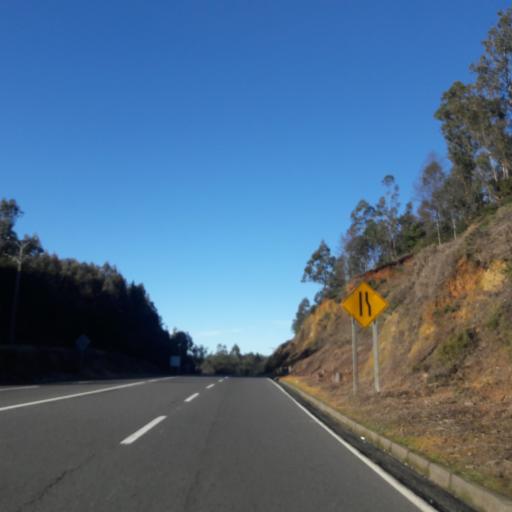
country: CL
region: Biobio
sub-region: Provincia de Biobio
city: La Laja
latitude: -37.2701
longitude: -72.9588
